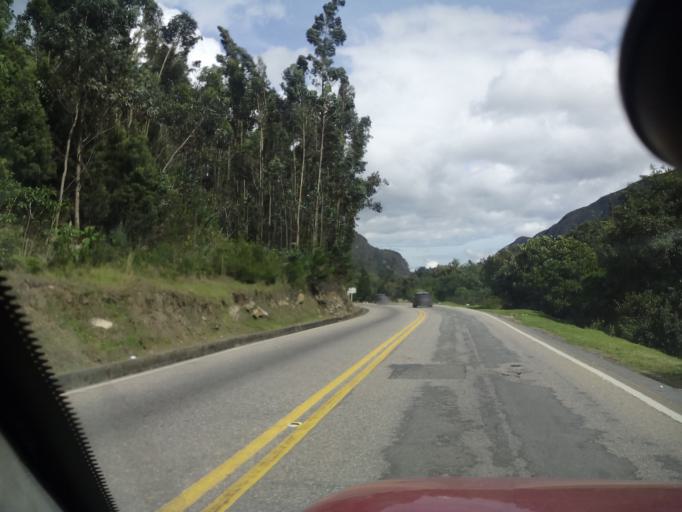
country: CO
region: Boyaca
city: Arcabuco
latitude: 5.7300
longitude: -73.3966
